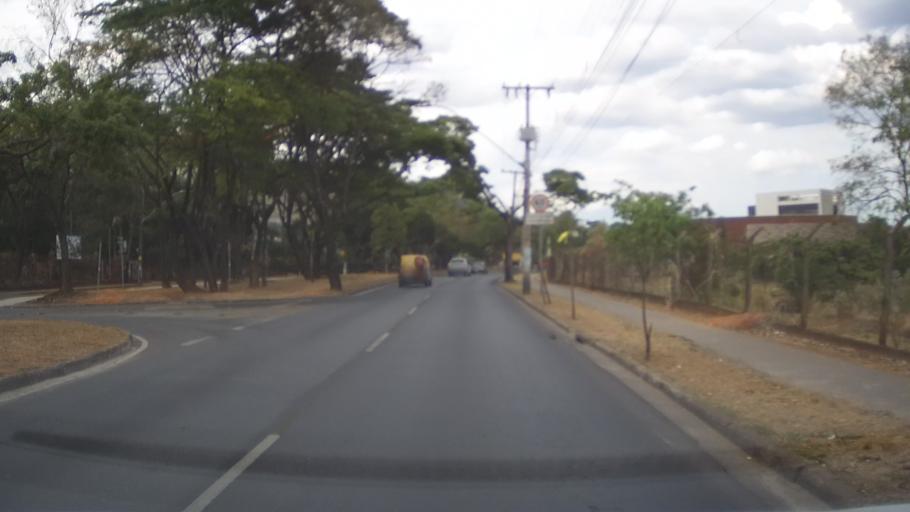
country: BR
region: Minas Gerais
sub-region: Belo Horizonte
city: Belo Horizonte
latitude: -19.8865
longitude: -43.9178
